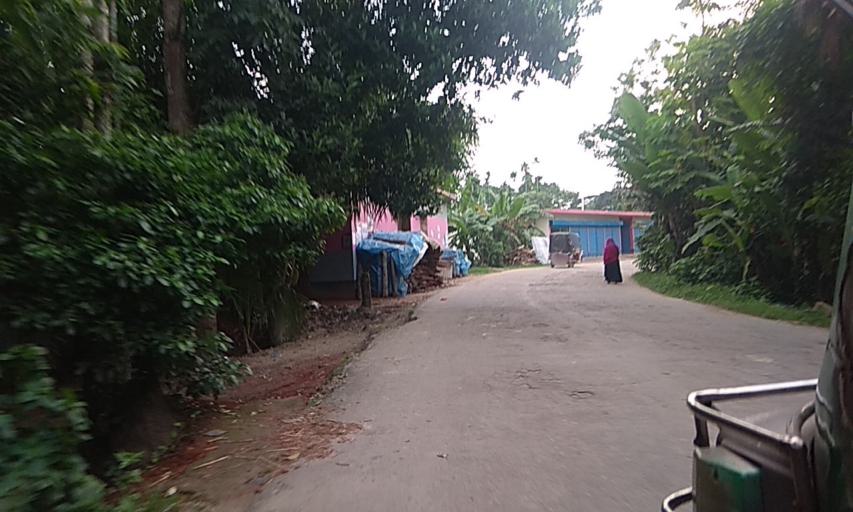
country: BD
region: Dhaka
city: Dohar
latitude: 23.4566
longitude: 90.0049
